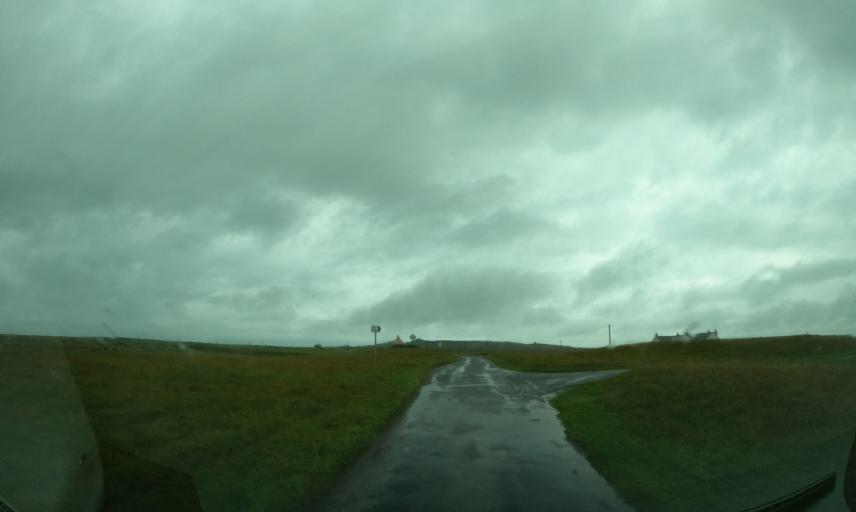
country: GB
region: Scotland
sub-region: Eilean Siar
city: Barra
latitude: 56.5152
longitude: -6.8157
